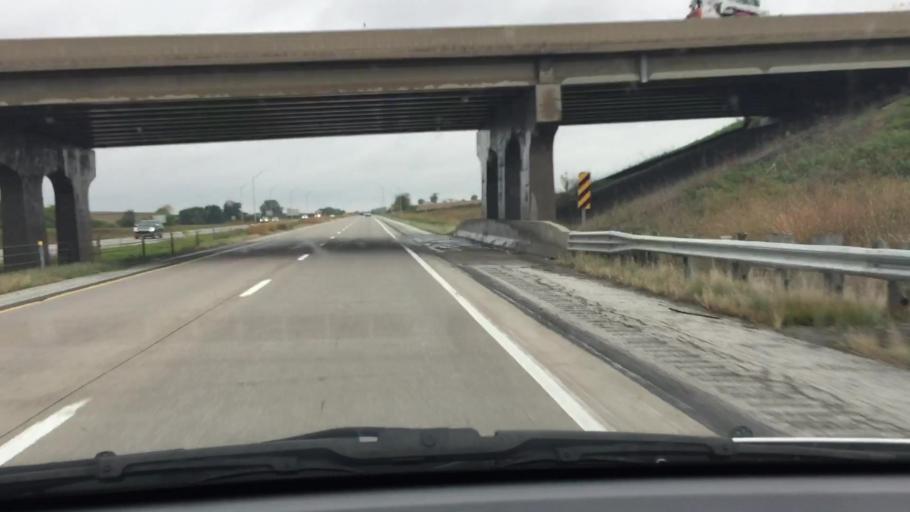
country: US
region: Iowa
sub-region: Iowa County
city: Williamsburg
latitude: 41.6878
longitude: -91.9108
